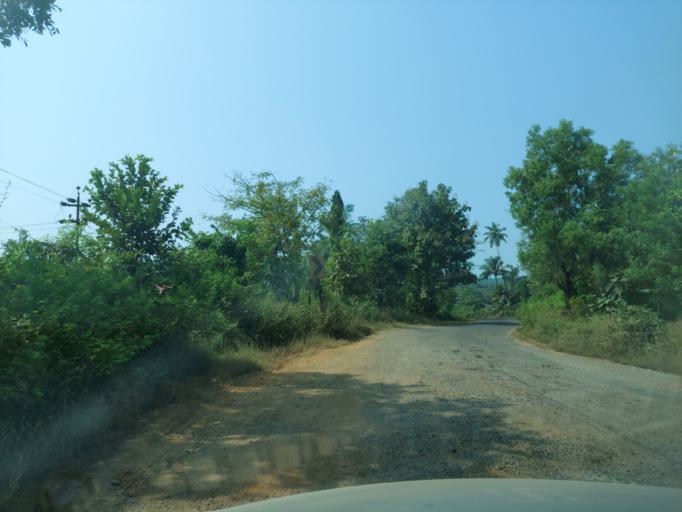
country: IN
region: Maharashtra
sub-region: Sindhudurg
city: Kudal
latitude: 15.9735
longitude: 73.6103
